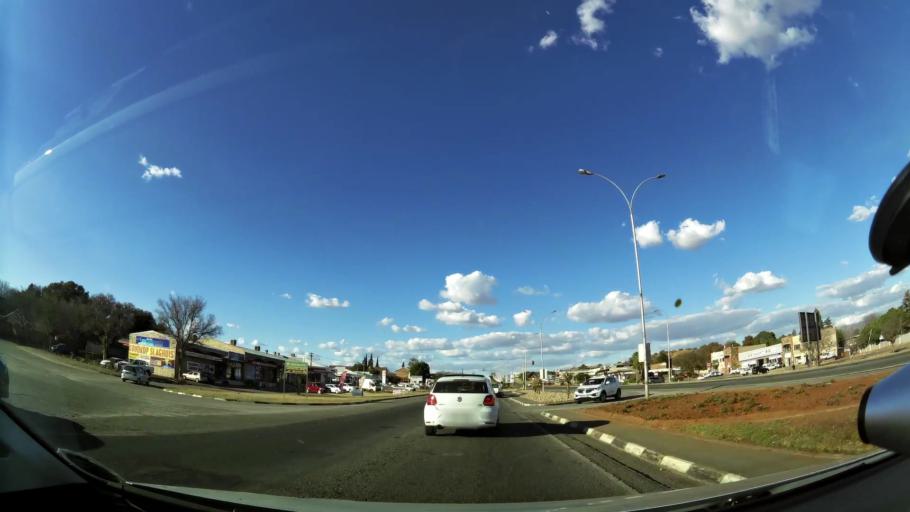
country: ZA
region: North-West
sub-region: Dr Kenneth Kaunda District Municipality
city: Klerksdorp
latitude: -26.8547
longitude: 26.6805
